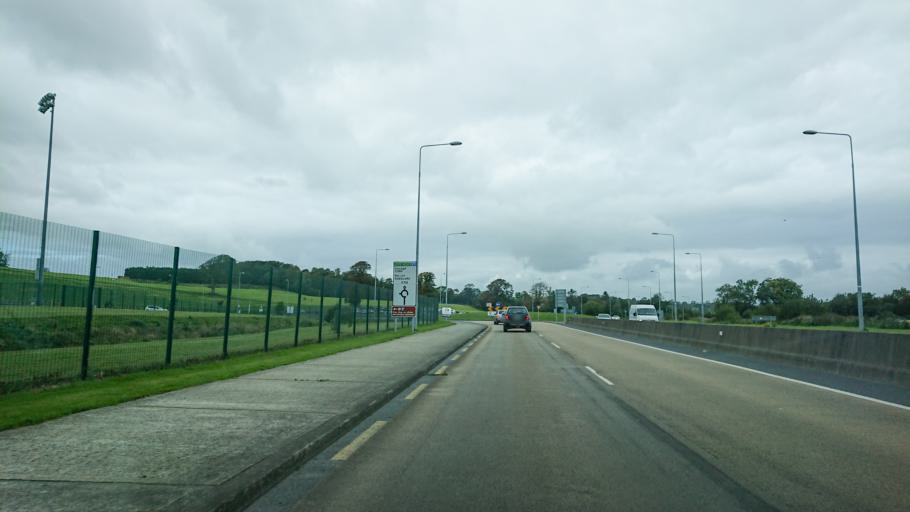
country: IE
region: Munster
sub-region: Waterford
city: Waterford
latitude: 52.2530
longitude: -7.1775
